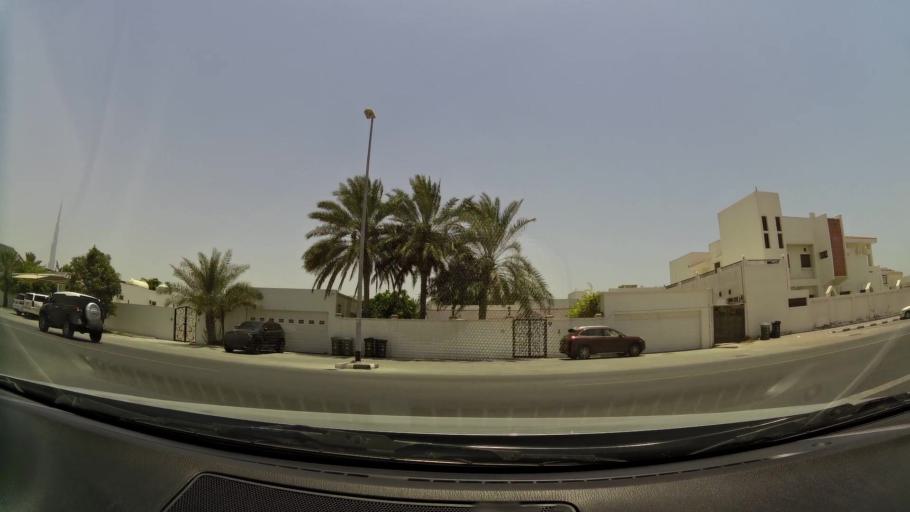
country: AE
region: Dubai
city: Dubai
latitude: 25.2263
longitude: 55.2621
